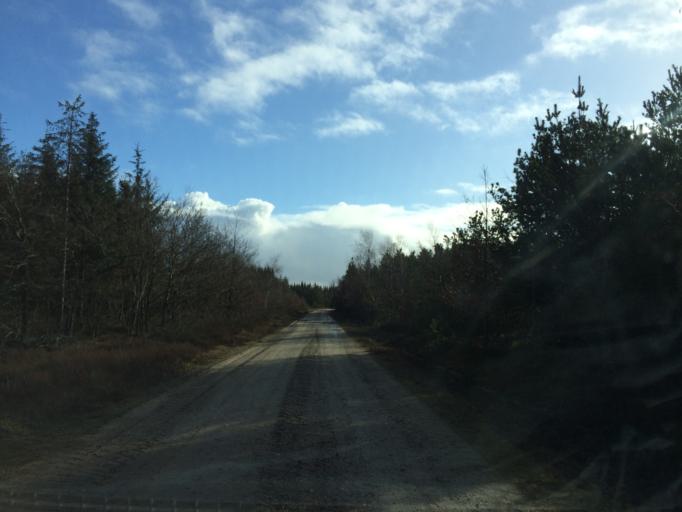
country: DK
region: Central Jutland
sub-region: Holstebro Kommune
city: Ulfborg
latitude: 56.2769
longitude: 8.3709
